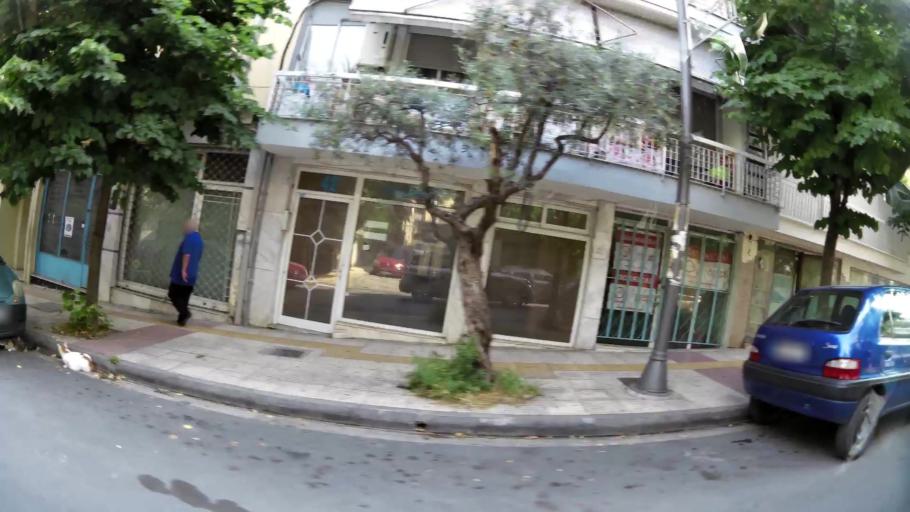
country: GR
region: Central Macedonia
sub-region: Nomos Thessalonikis
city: Sykies
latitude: 40.6494
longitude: 22.9467
